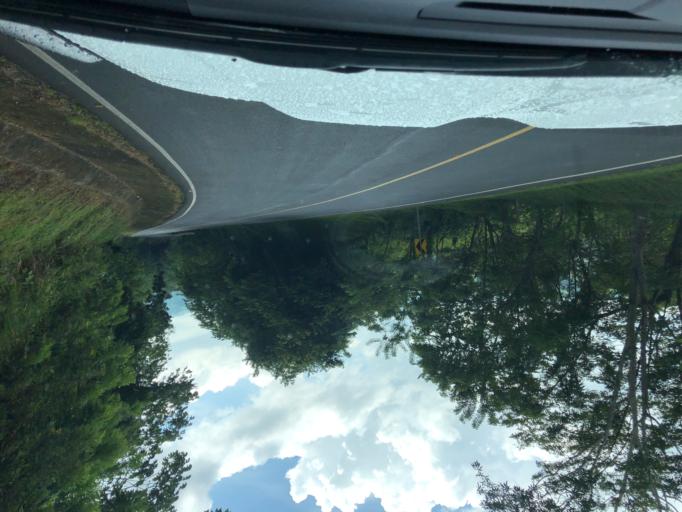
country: NI
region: Chontales
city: Villa Sandino
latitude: 12.0064
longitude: -84.9370
